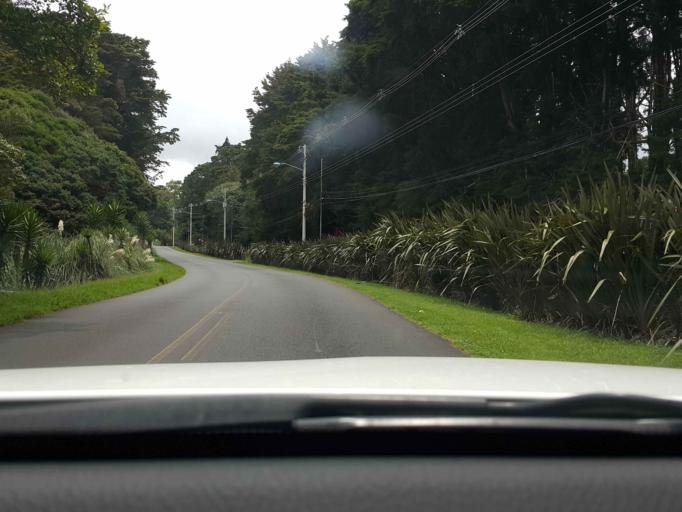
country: CR
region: Heredia
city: San Josecito
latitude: 10.0526
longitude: -84.0859
